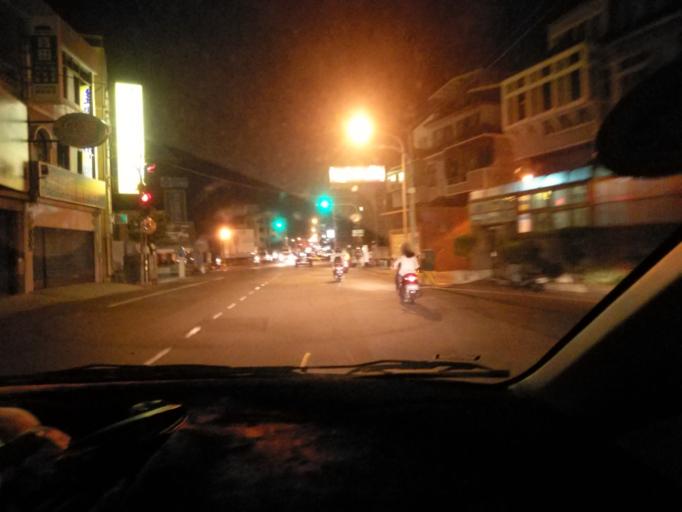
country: TW
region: Taiwan
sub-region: Miaoli
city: Miaoli
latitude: 24.6942
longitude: 120.8705
